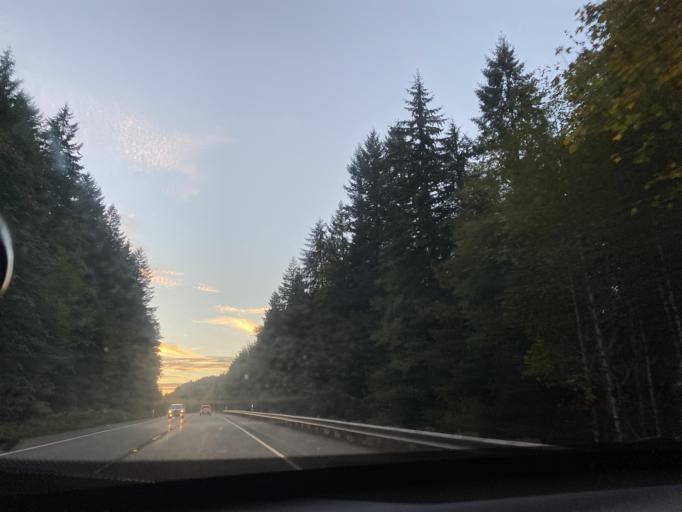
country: US
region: Washington
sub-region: Clallam County
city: Port Angeles
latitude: 48.0709
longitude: -123.6337
